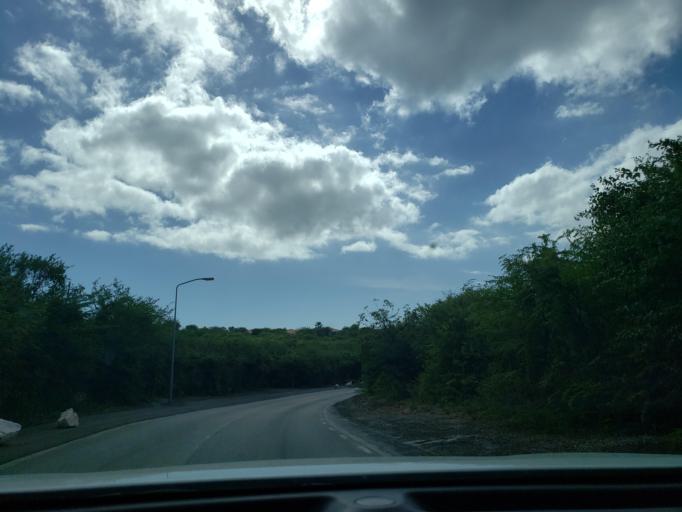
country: CW
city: Dorp Soto
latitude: 12.2065
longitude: -69.0759
